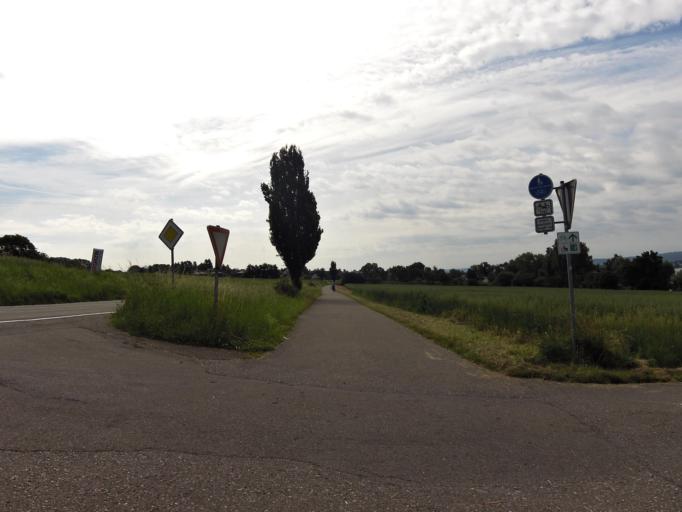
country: DE
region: Baden-Wuerttemberg
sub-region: Freiburg Region
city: Allensbach
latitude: 47.7239
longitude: 9.0459
